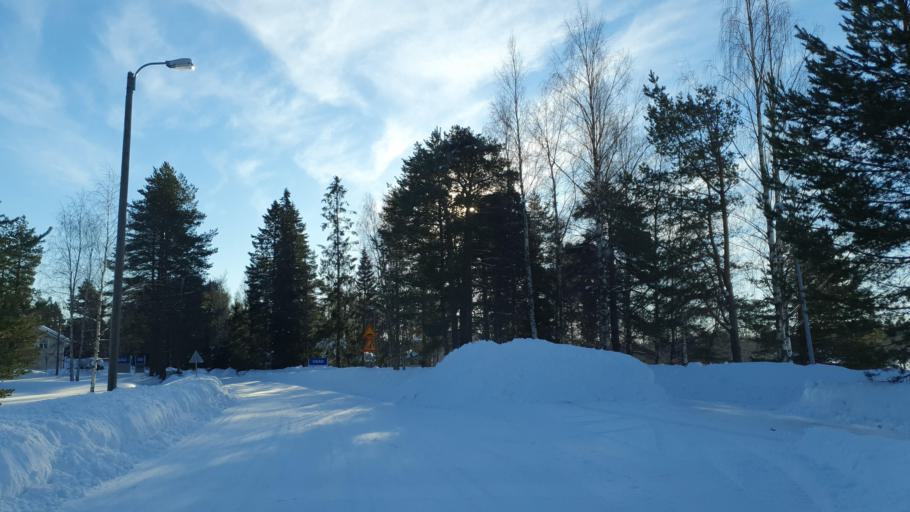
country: FI
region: Northern Ostrobothnia
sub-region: Oulu
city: Haukipudas
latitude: 65.1941
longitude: 25.4113
